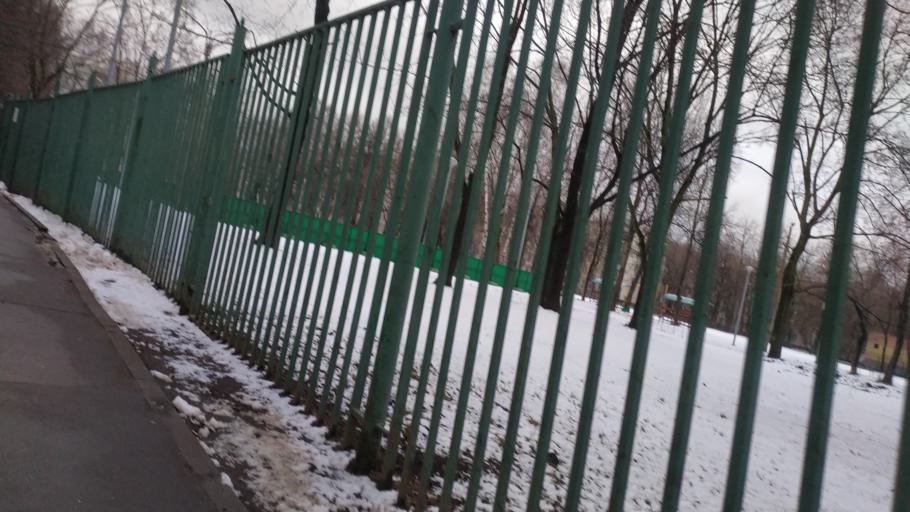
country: RU
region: Moscow
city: Novokuz'minki
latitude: 55.7069
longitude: 37.7715
